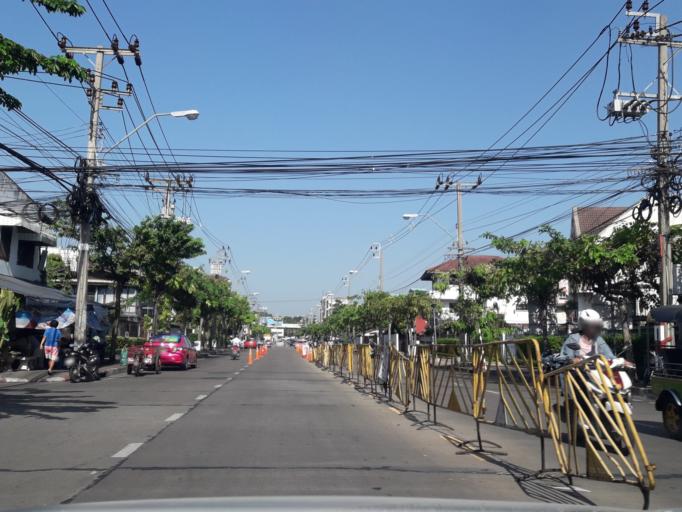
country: TH
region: Bangkok
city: Thon Buri
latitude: 13.7365
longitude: 100.4931
